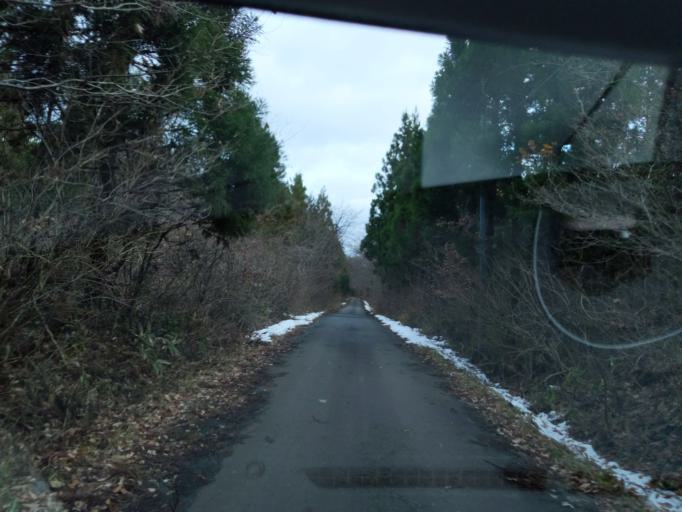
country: JP
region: Iwate
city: Ichinoseki
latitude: 38.9766
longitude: 141.0408
